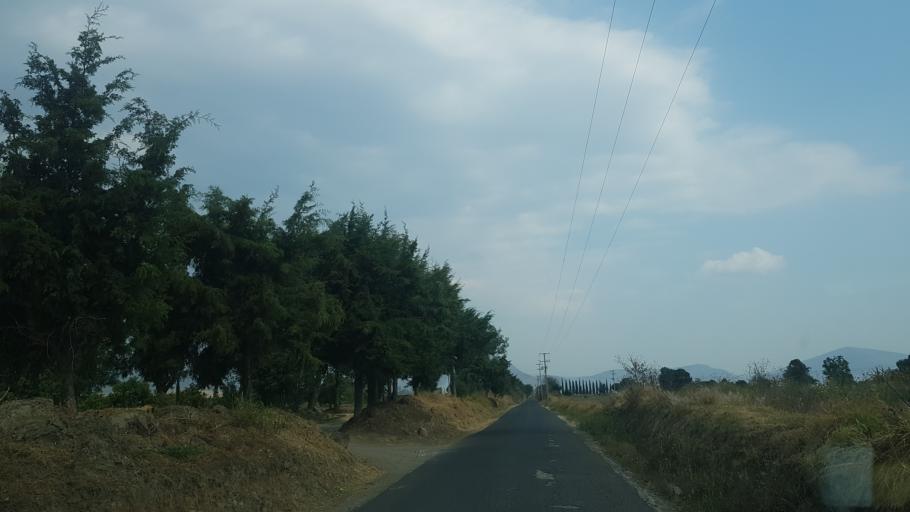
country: MX
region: Puebla
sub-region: Santa Isabel Cholula
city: Santa Ana Acozautla
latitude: 18.9564
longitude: -98.4020
